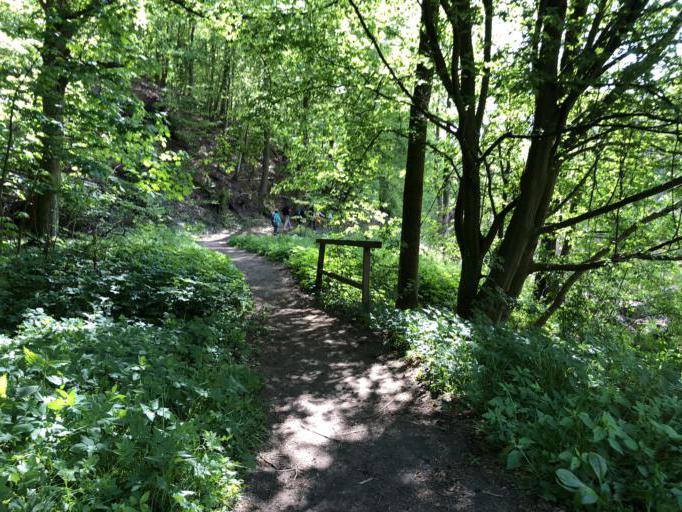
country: DE
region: Saxony
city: Wechselburg
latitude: 51.0075
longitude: 12.7811
